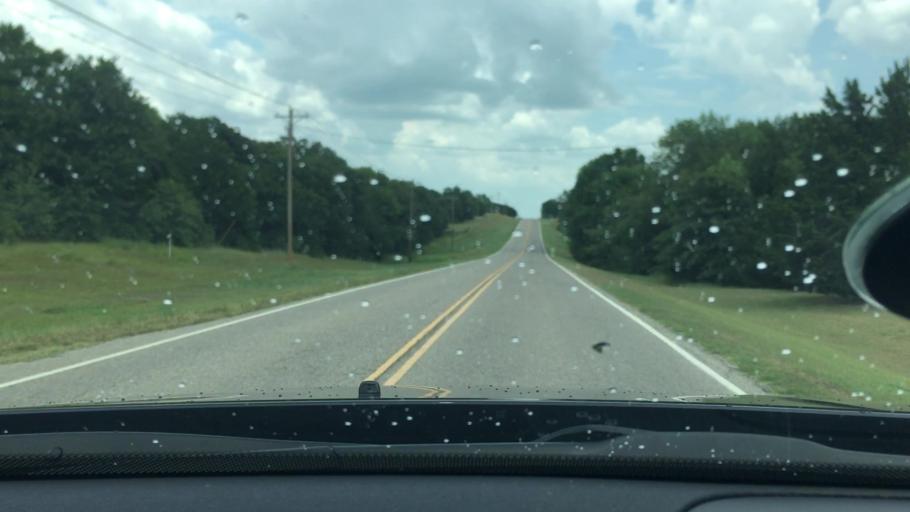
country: US
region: Oklahoma
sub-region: Love County
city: Marietta
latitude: 33.9506
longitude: -97.0330
